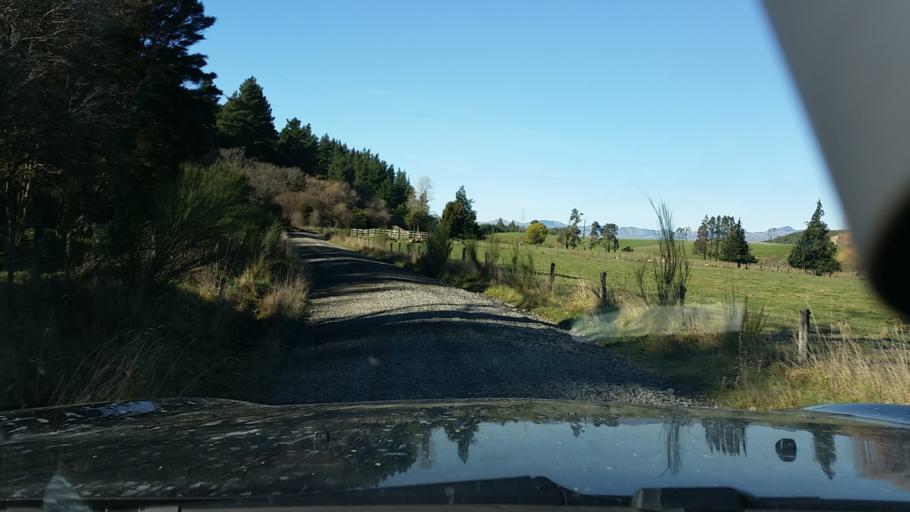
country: NZ
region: Marlborough
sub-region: Marlborough District
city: Blenheim
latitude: -41.4607
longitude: 173.7874
